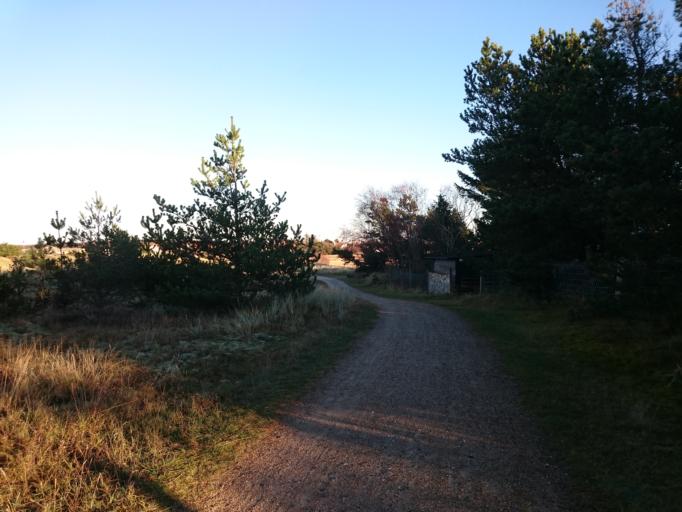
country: DK
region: North Denmark
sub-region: Frederikshavn Kommune
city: Skagen
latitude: 57.7153
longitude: 10.5609
